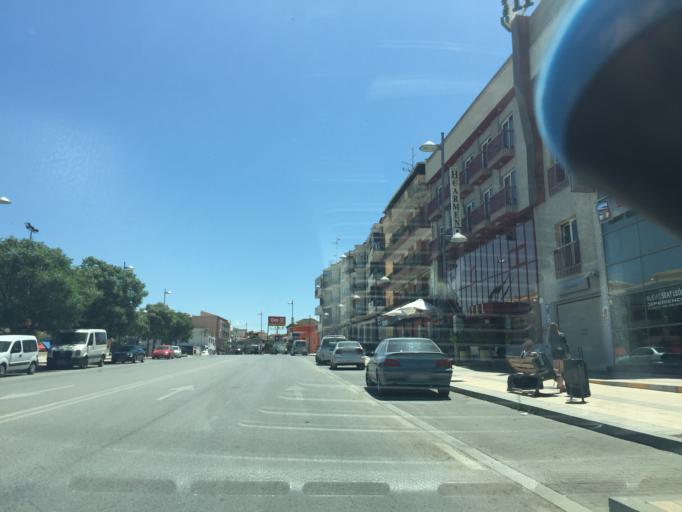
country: ES
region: Andalusia
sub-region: Provincia de Granada
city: Guadix
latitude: 37.3062
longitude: -3.1449
